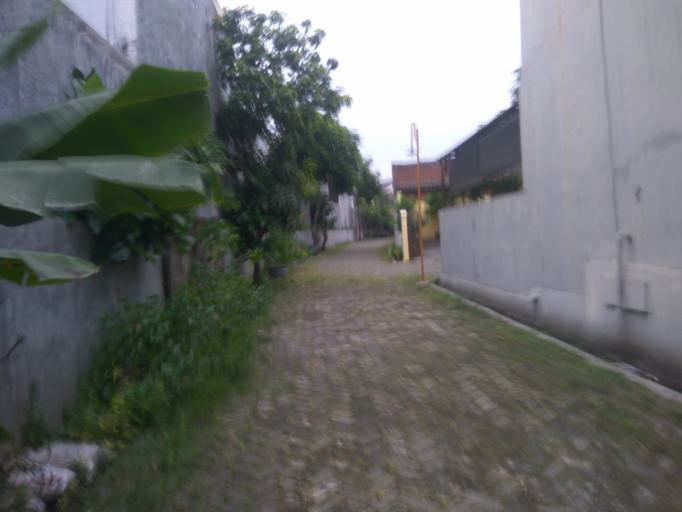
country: ID
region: Central Java
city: Mranggen
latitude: -7.0255
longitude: 110.4632
